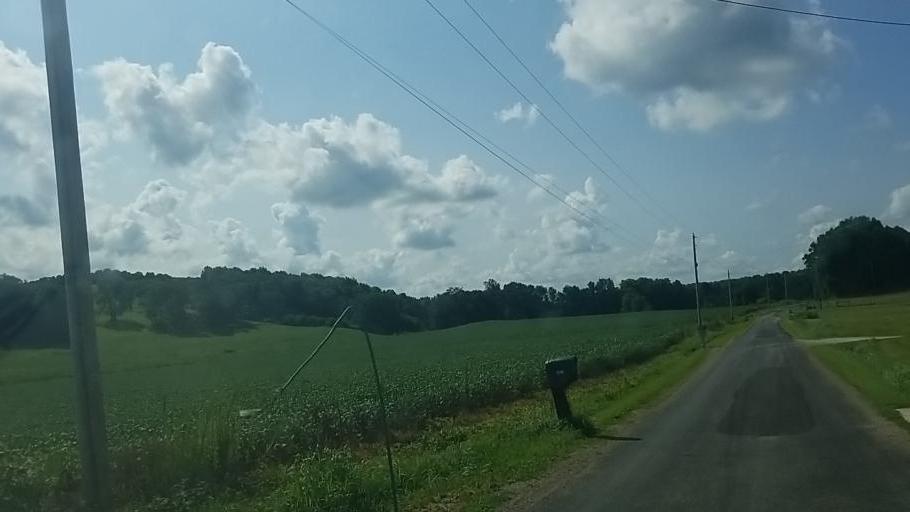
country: US
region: Ohio
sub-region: Ashland County
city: Ashland
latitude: 40.7537
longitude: -82.2995
